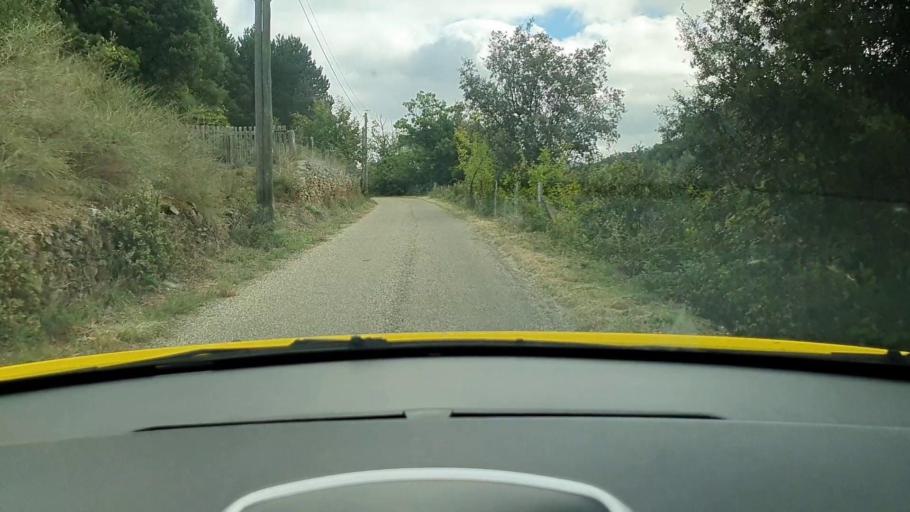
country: FR
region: Languedoc-Roussillon
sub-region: Departement du Gard
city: Sumene
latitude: 44.0162
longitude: 3.6667
